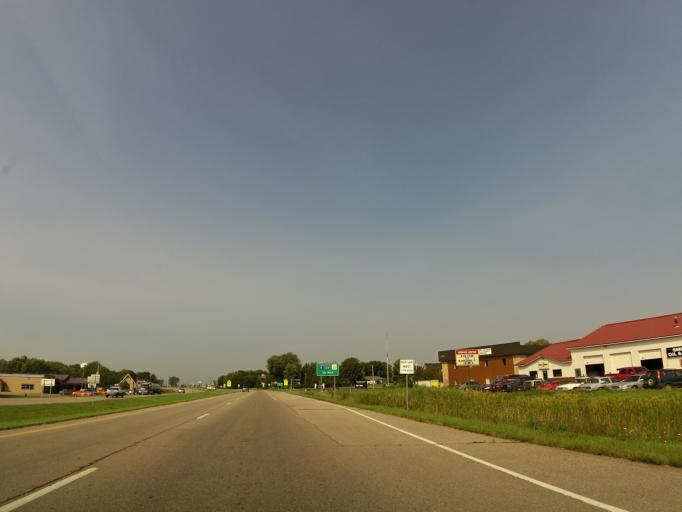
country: US
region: Minnesota
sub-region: Carver County
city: Norwood Young America
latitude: 44.7715
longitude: -93.9201
